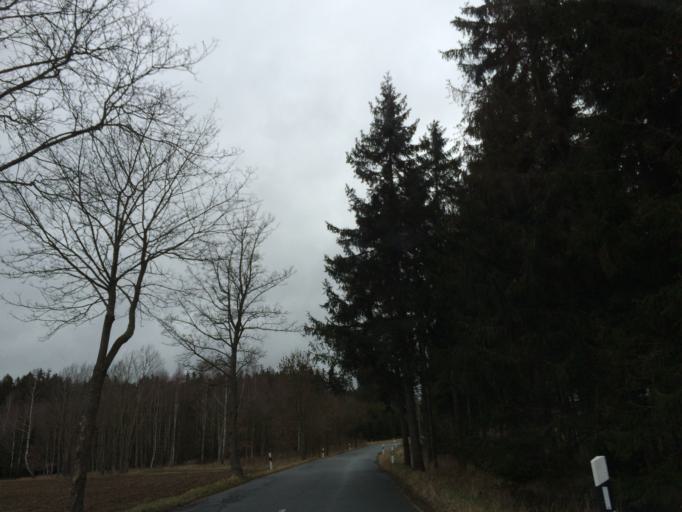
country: DE
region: Thuringia
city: Knau
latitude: 50.6658
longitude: 11.7178
